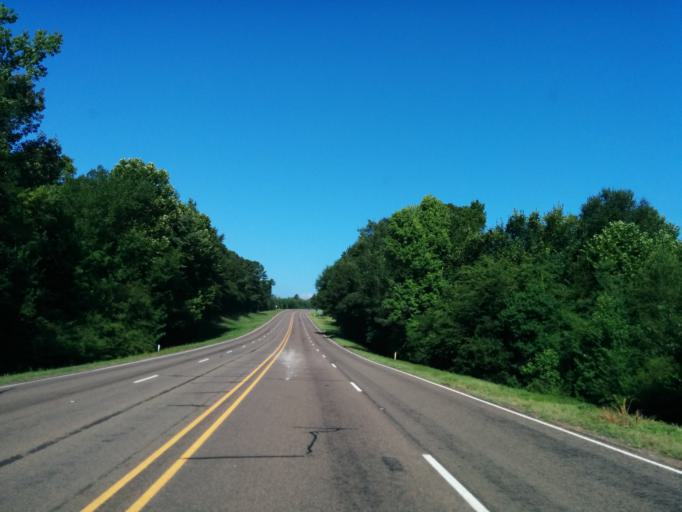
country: US
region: Texas
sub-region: Sabine County
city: Milam
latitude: 31.4314
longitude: -93.8203
